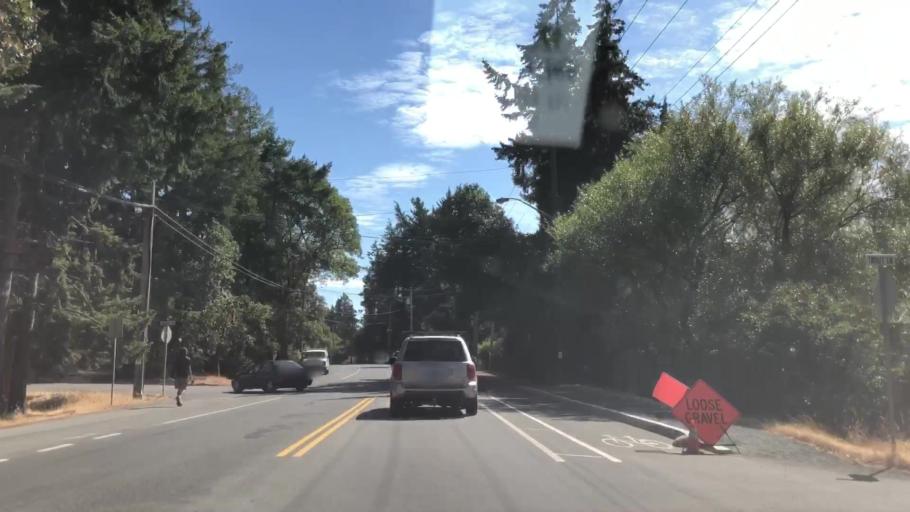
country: CA
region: British Columbia
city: Colwood
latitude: 48.4319
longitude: -123.4954
